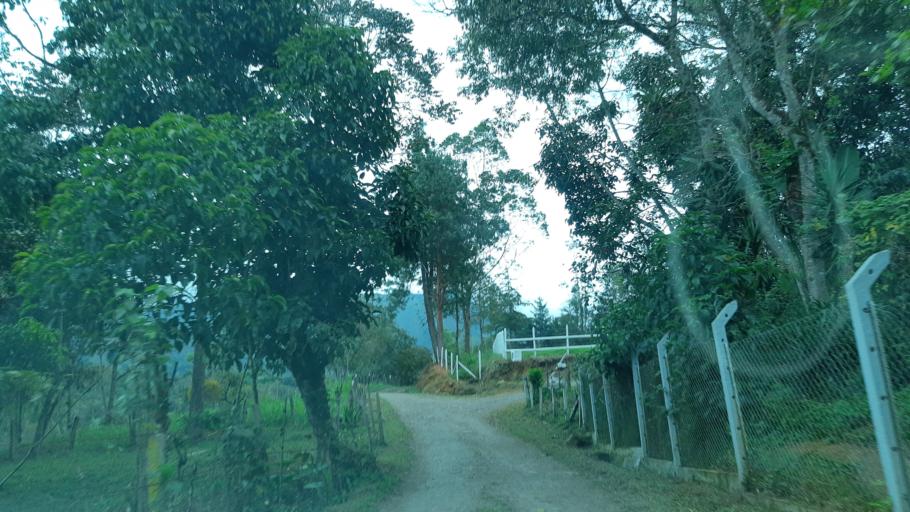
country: CO
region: Boyaca
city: Garagoa
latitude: 5.0840
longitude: -73.3570
